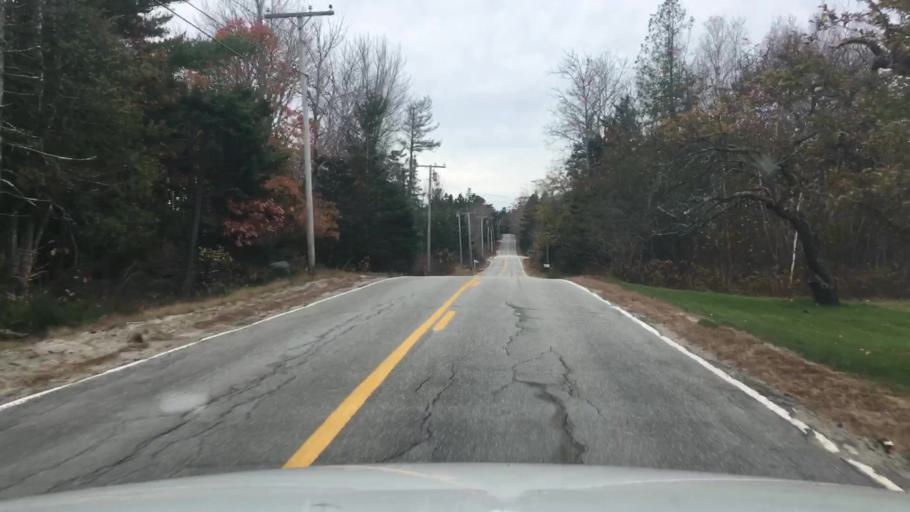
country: US
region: Maine
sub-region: Hancock County
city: Sedgwick
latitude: 44.3386
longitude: -68.5626
